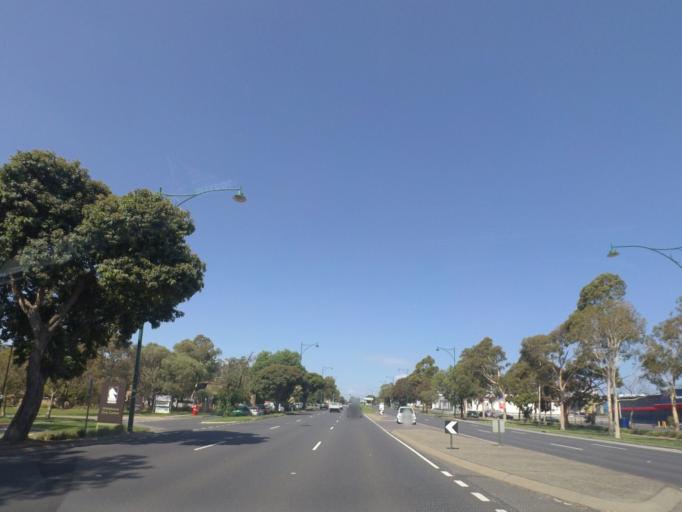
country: AU
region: Victoria
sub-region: Whitehorse
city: Nunawading
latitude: -37.8179
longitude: 145.1823
